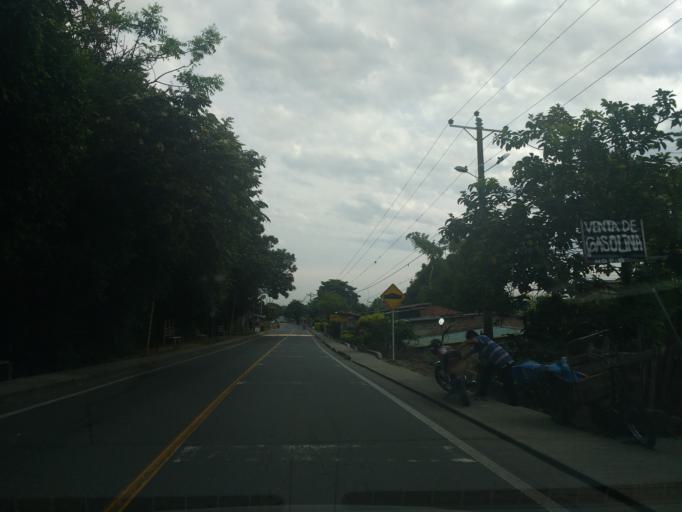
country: CO
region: Cauca
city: Miranda
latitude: 3.2821
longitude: -76.2236
